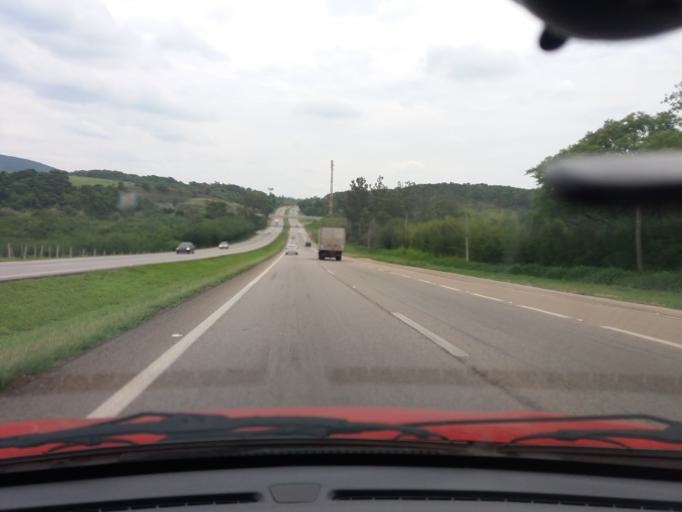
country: BR
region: Sao Paulo
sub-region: Itupeva
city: Itupeva
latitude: -23.1932
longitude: -46.9918
